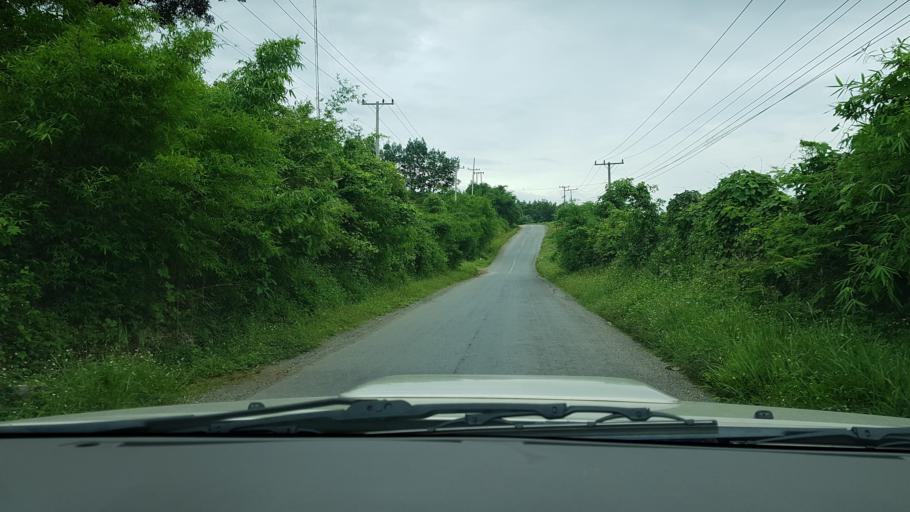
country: LA
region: Loungnamtha
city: Muang Nale
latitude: 20.1746
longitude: 101.5133
